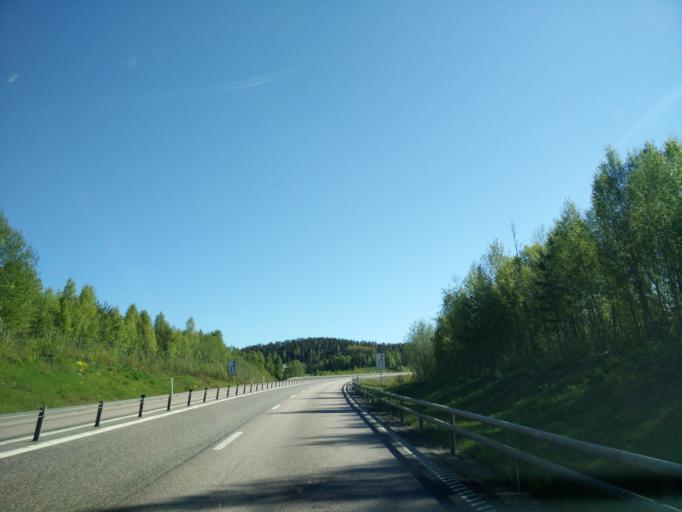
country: SE
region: Vaesternorrland
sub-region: Haernoesands Kommun
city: Haernoesand
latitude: 62.8390
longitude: 17.9724
